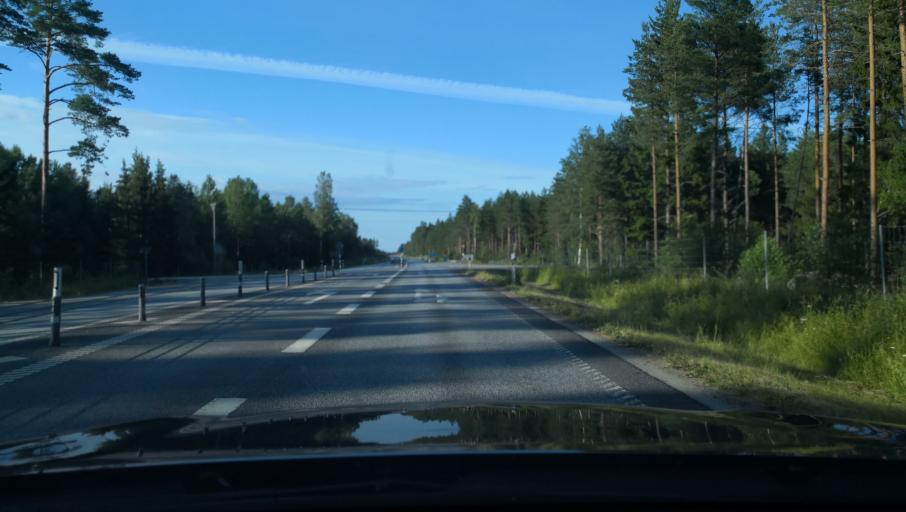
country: SE
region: Uppsala
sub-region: Uppsala Kommun
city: Vattholma
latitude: 59.9838
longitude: 17.9448
